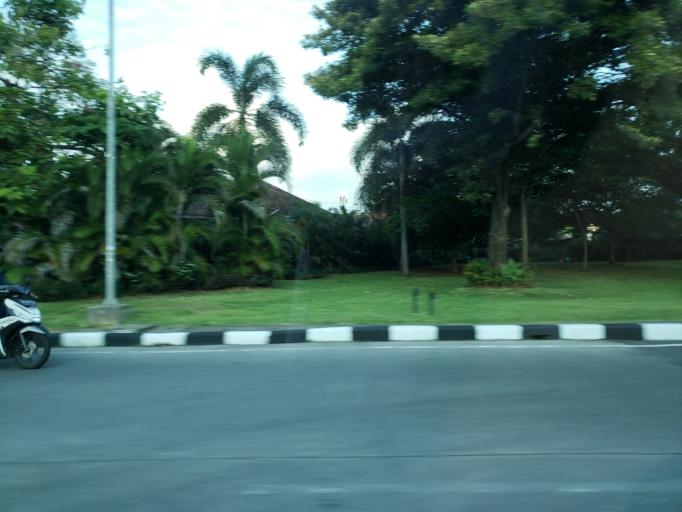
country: ID
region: Bali
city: Kelanabian
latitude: -8.7433
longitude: 115.1677
